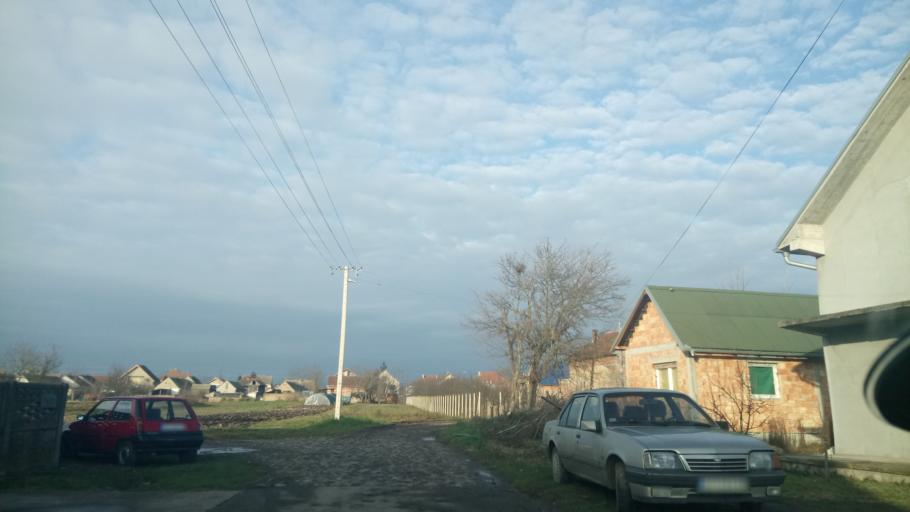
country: RS
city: Vojka
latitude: 44.9335
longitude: 20.1485
